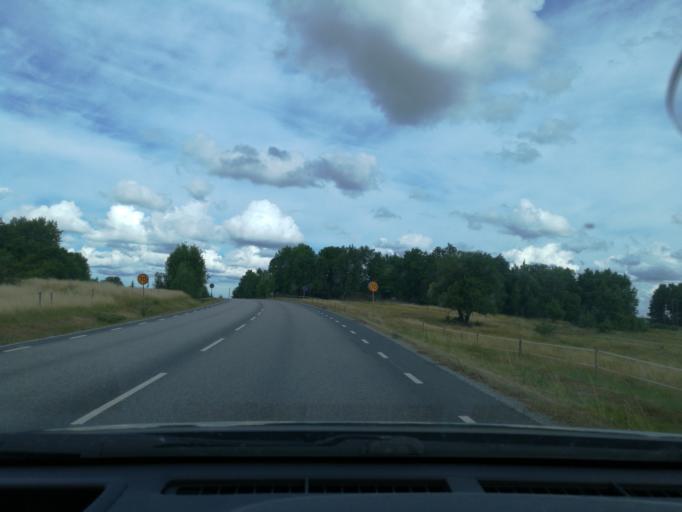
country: SE
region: Stockholm
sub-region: Sigtuna Kommun
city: Marsta
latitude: 59.6389
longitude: 17.8601
